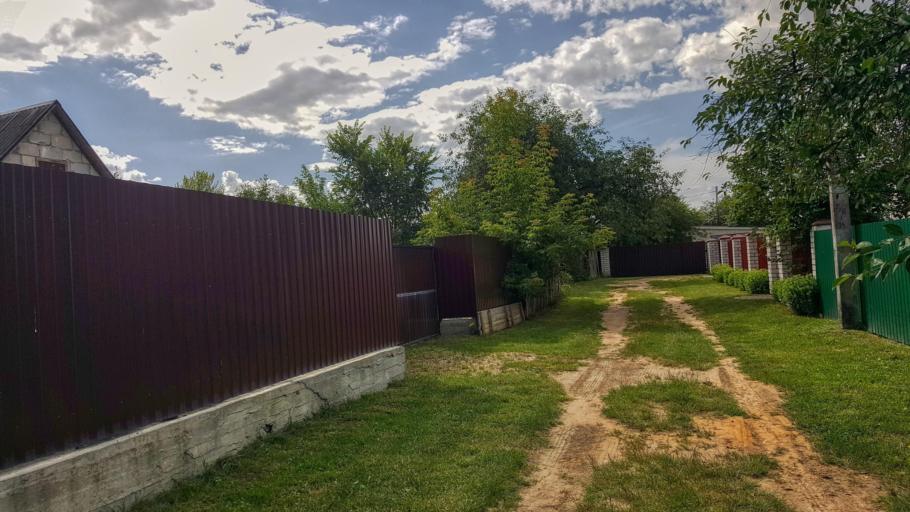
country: BY
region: Brest
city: Kamyanyets
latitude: 52.4029
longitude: 23.8342
